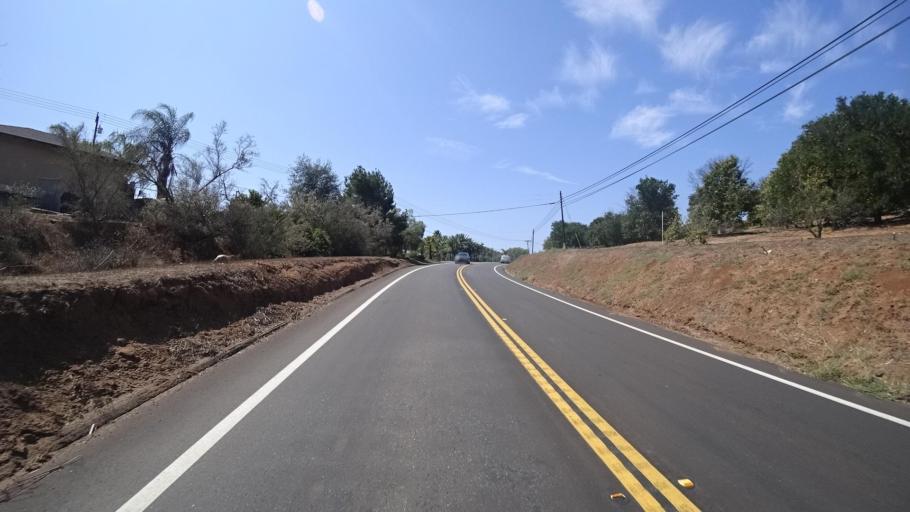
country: US
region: California
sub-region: San Diego County
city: Hidden Meadows
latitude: 33.2567
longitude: -117.0769
